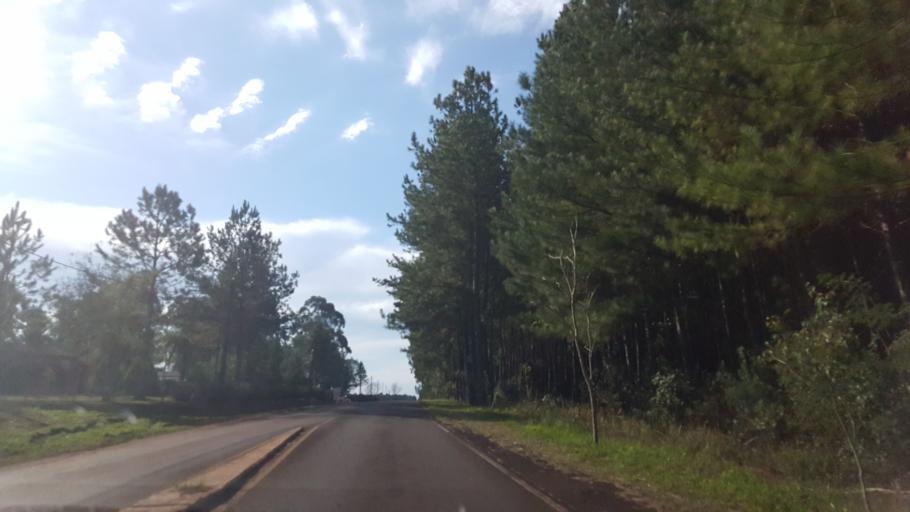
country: AR
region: Misiones
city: Jardin America
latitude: -27.0134
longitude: -55.1899
